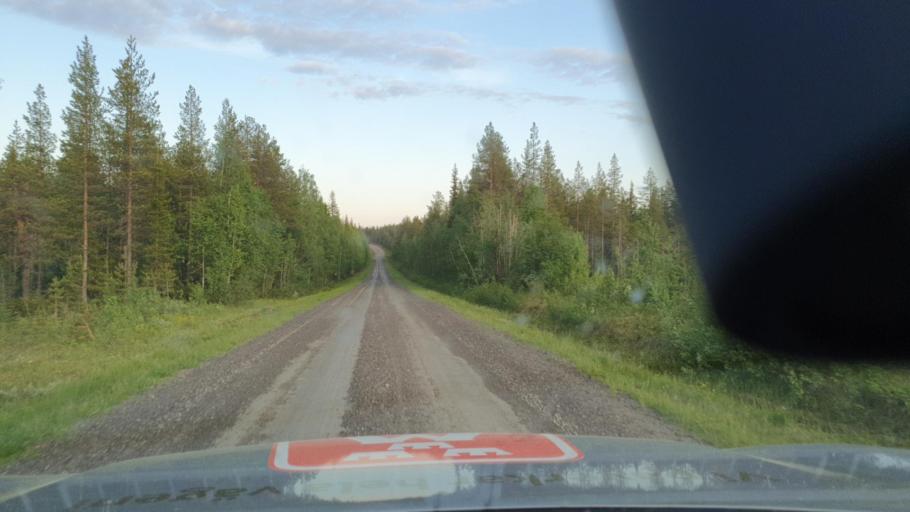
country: SE
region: Norrbotten
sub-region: Bodens Kommun
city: Boden
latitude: 66.4591
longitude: 21.6462
